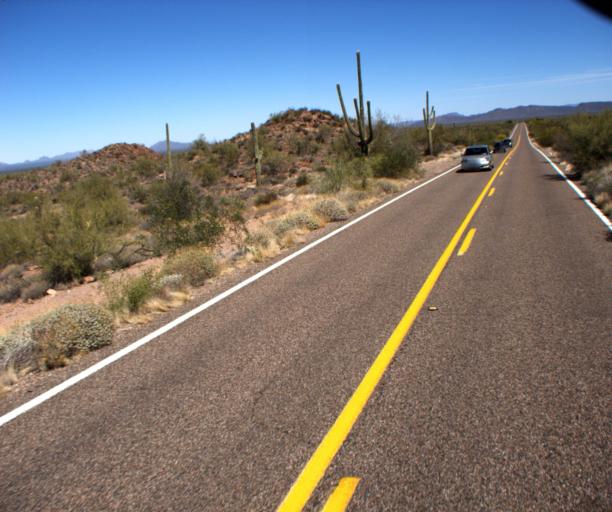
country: MX
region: Sonora
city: Sonoyta
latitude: 32.0862
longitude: -112.7769
